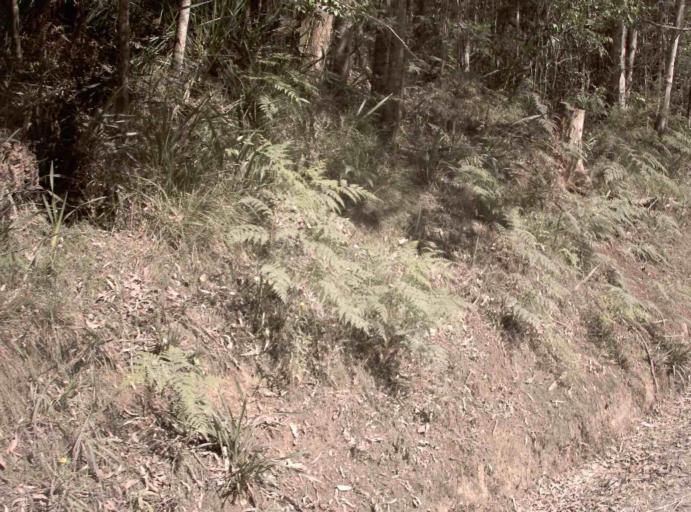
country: AU
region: New South Wales
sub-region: Bombala
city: Bombala
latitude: -37.2195
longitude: 148.7471
